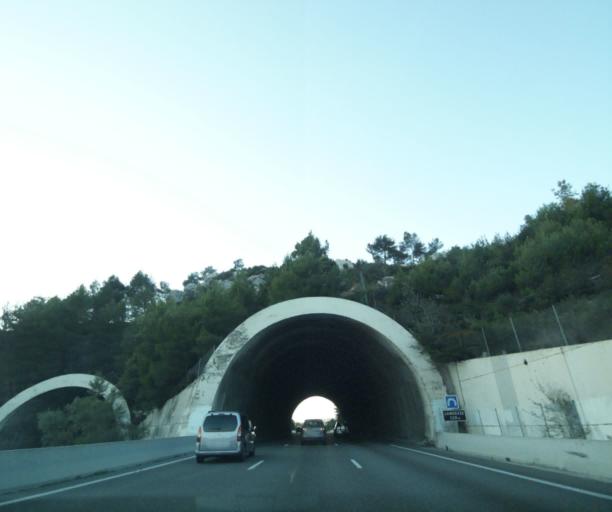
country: FR
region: Provence-Alpes-Cote d'Azur
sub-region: Departement des Bouches-du-Rhone
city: Le Tholonet
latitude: 43.5054
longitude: 5.5101
